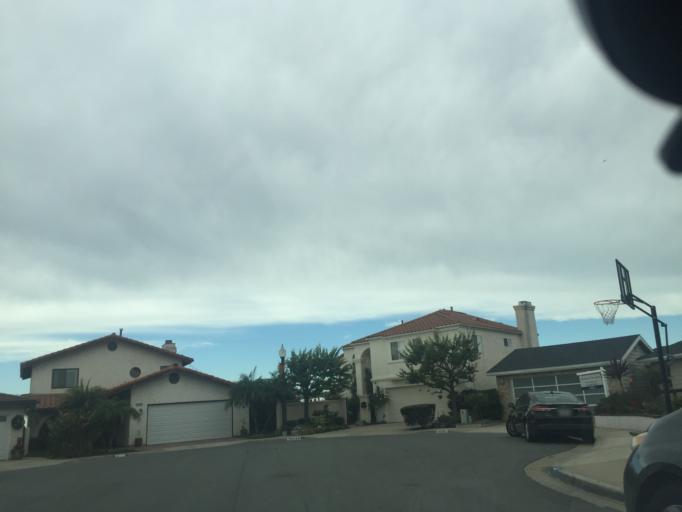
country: US
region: California
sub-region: San Diego County
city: Lemon Grove
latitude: 32.7682
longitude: -117.0944
